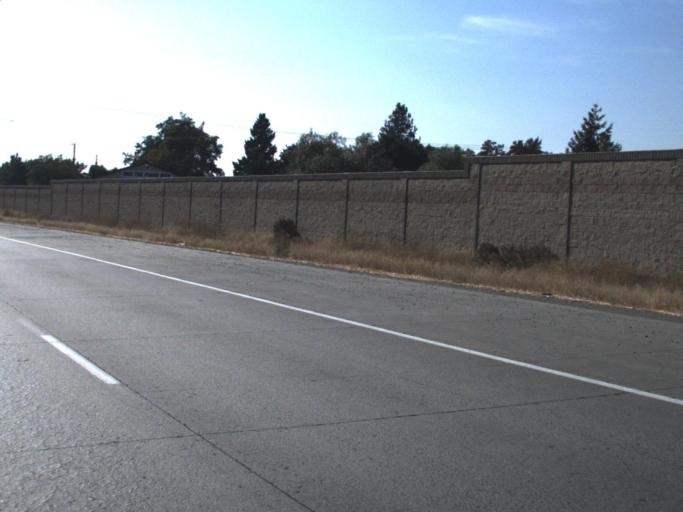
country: US
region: Washington
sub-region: Spokane County
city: Millwood
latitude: 47.6722
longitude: -117.2928
